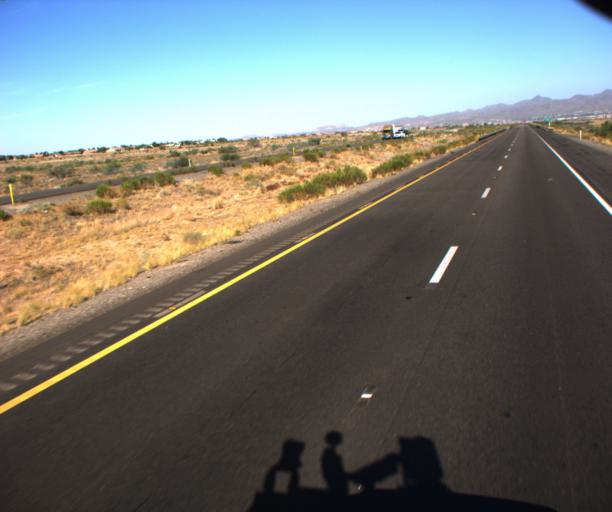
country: US
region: Arizona
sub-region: Mohave County
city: New Kingman-Butler
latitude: 35.2064
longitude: -113.9495
